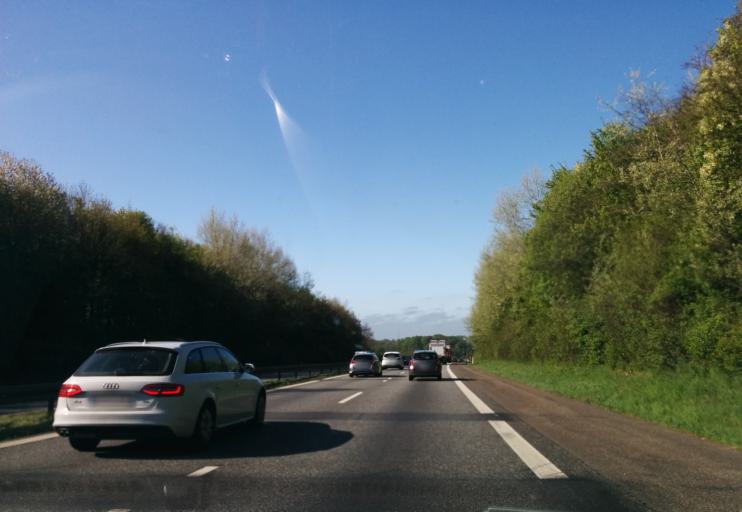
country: DK
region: Central Jutland
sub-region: Horsens Kommune
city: Horsens
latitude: 55.9548
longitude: 9.8360
